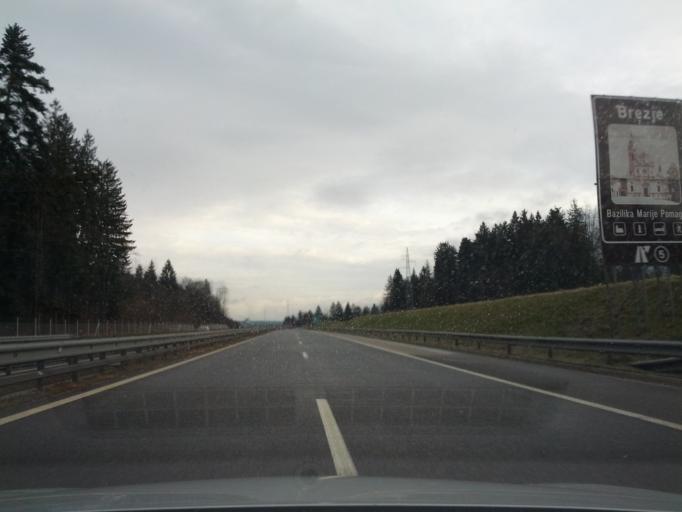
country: SI
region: Radovljica
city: Radovljica
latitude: 46.3356
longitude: 14.1966
